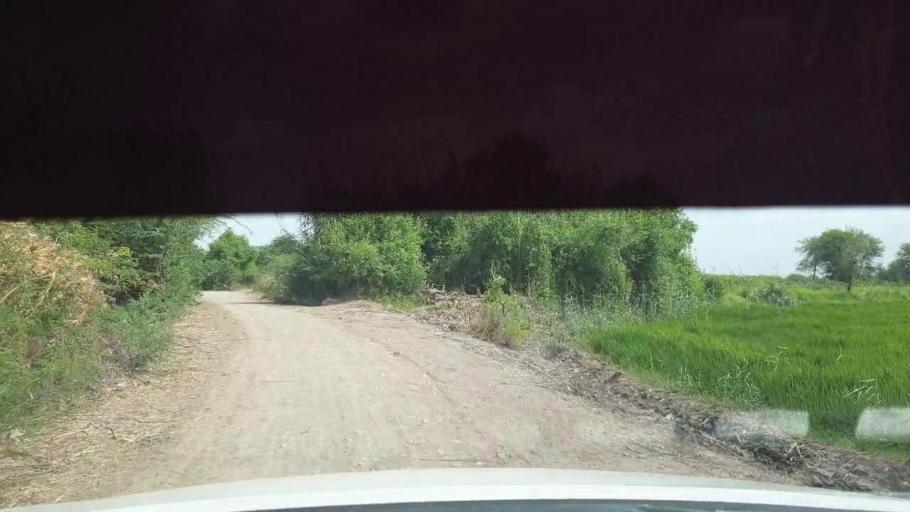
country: PK
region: Sindh
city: Kadhan
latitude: 24.6128
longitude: 69.0259
